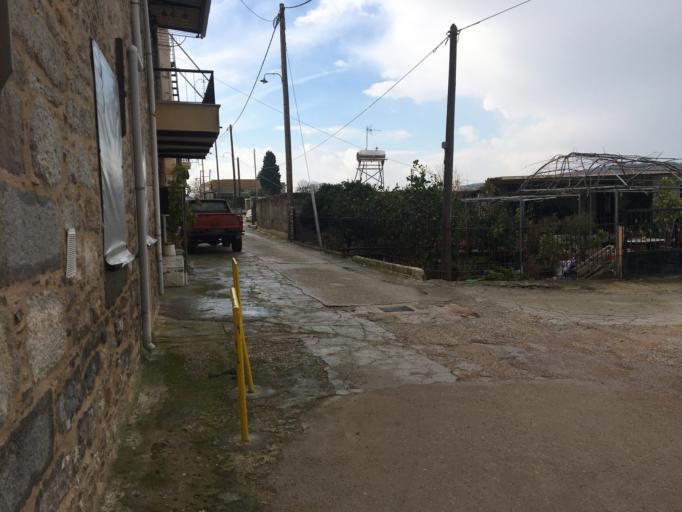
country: GR
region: North Aegean
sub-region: Chios
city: Thymiana
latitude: 38.2479
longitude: 25.9420
